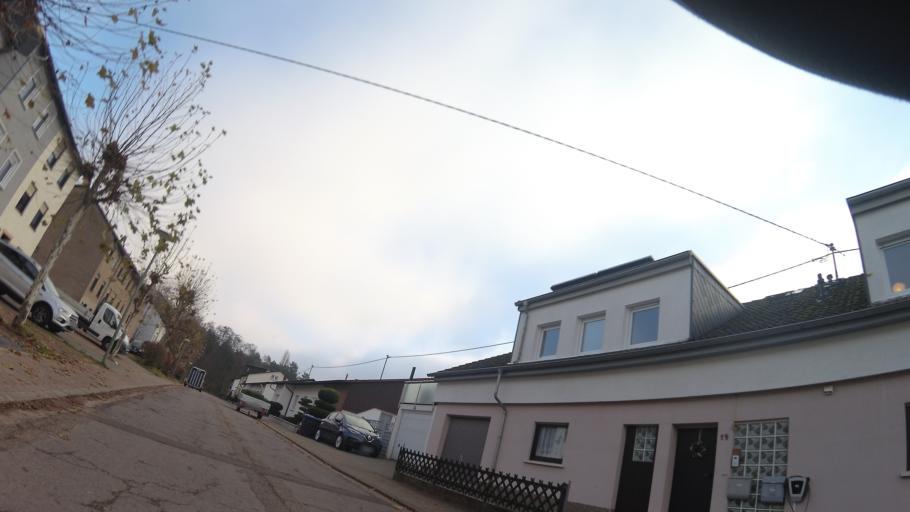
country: DE
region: Saarland
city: Ensdorf
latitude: 49.3007
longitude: 6.7829
